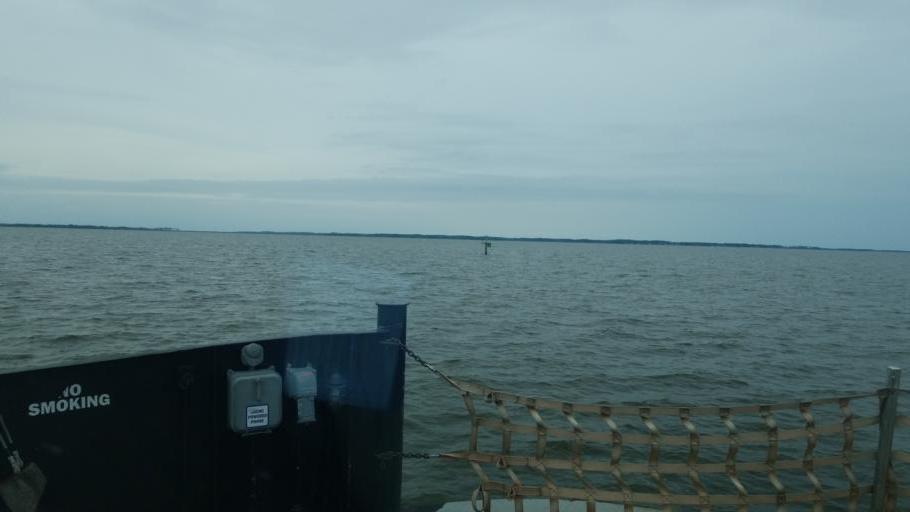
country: US
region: North Carolina
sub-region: Currituck County
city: Currituck
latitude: 36.4592
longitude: -75.9778
